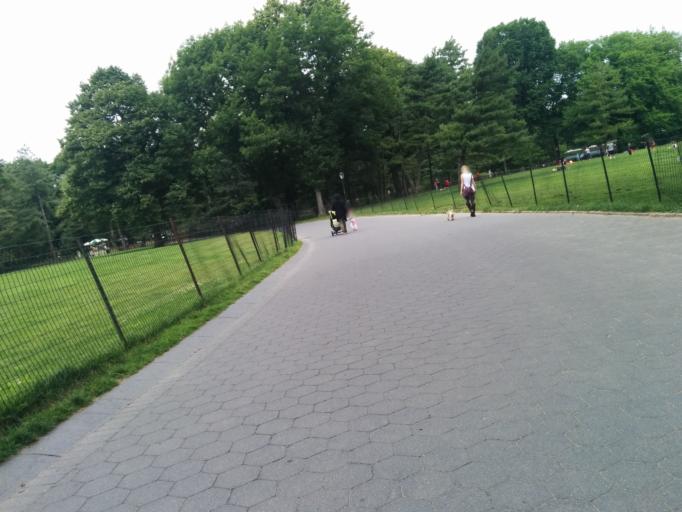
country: US
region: New York
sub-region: New York County
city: Manhattan
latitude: 40.7823
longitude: -73.9654
